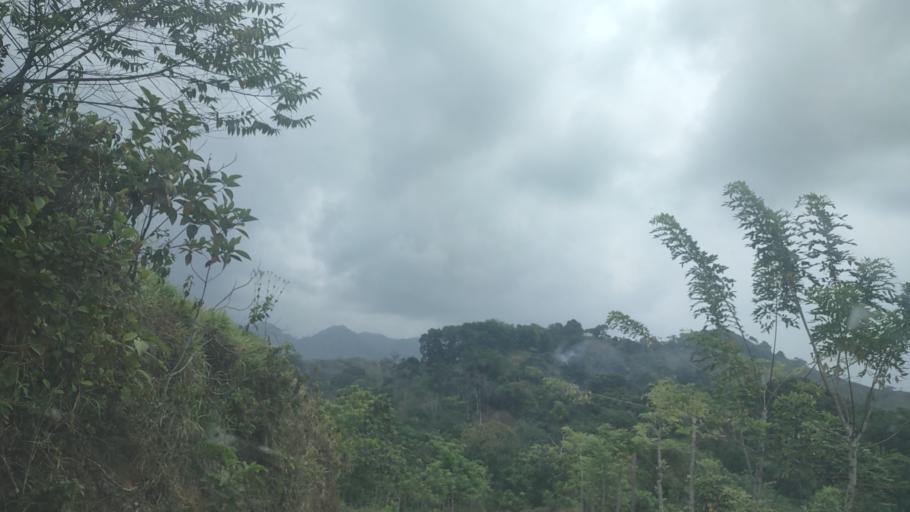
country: MX
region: Tabasco
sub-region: Huimanguillo
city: Francisco Rueda
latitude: 17.4423
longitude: -94.0273
